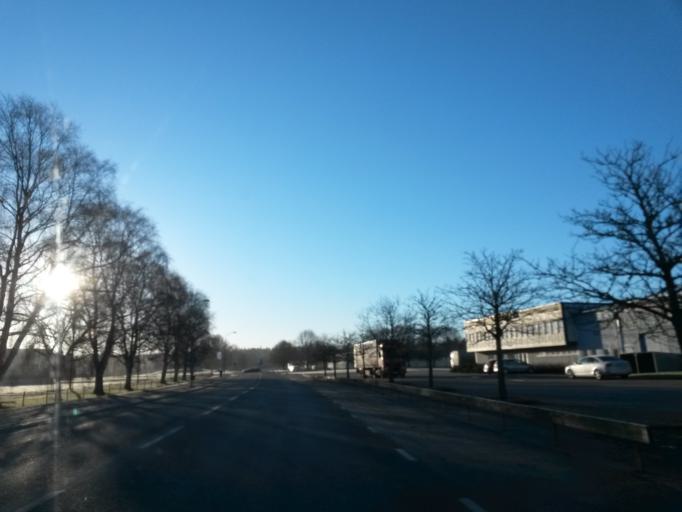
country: SE
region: Vaestra Goetaland
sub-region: Herrljunga Kommun
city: Herrljunga
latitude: 58.0754
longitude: 13.0183
